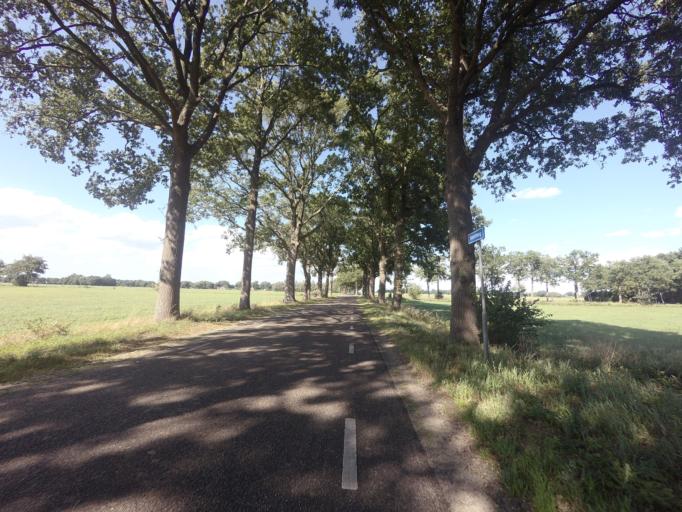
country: NL
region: Drenthe
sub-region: Gemeente Hoogeveen
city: Hoogeveen
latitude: 52.6246
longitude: 6.4823
